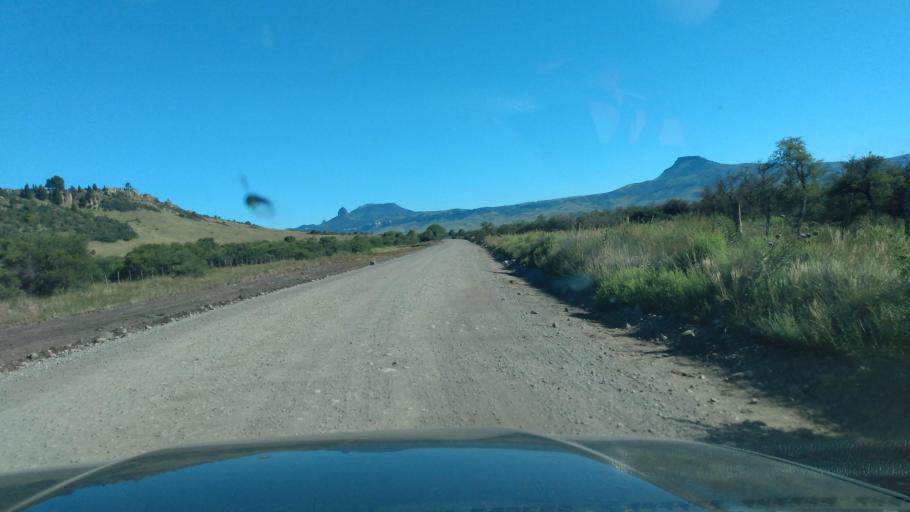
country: AR
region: Neuquen
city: Junin de los Andes
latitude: -39.8442
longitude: -71.1884
